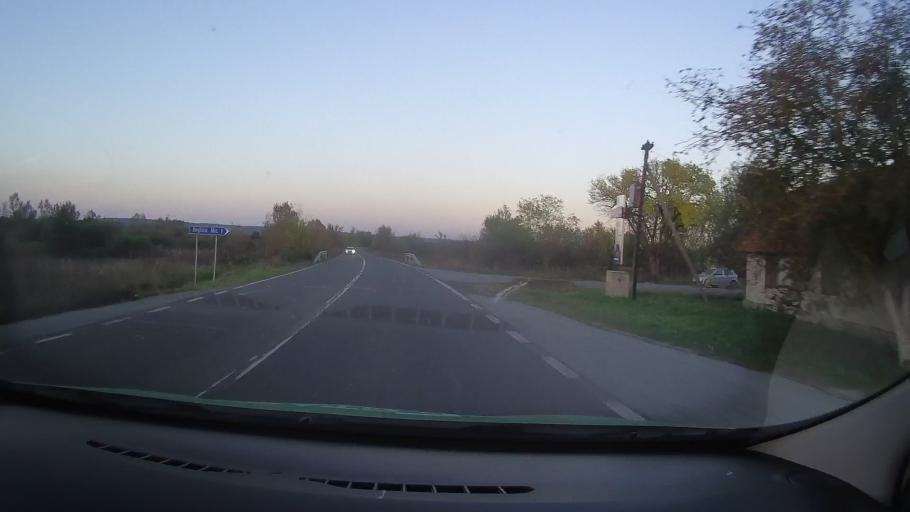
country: RO
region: Timis
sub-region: Comuna Dumbrava
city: Dumbrava
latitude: 45.8380
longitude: 22.1420
